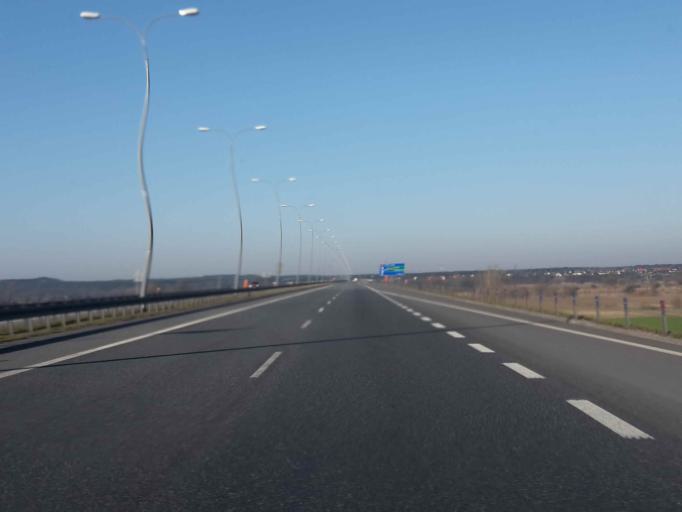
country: PL
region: Kujawsko-Pomorskie
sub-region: Powiat torunski
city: Lubicz Dolny
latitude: 52.9748
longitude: 18.7128
